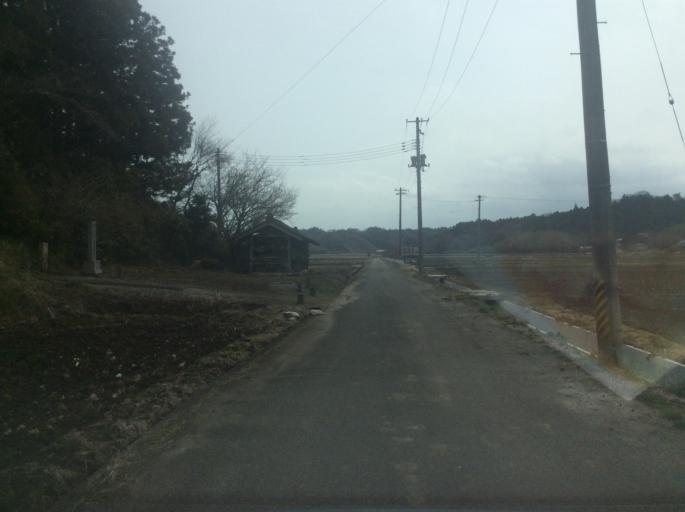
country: JP
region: Fukushima
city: Iwaki
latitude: 37.0990
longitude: 140.9409
